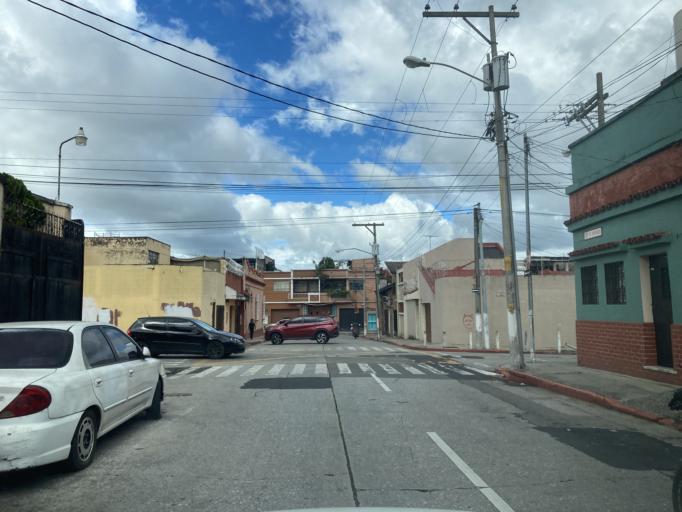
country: GT
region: Guatemala
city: Guatemala City
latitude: 14.6482
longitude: -90.5140
